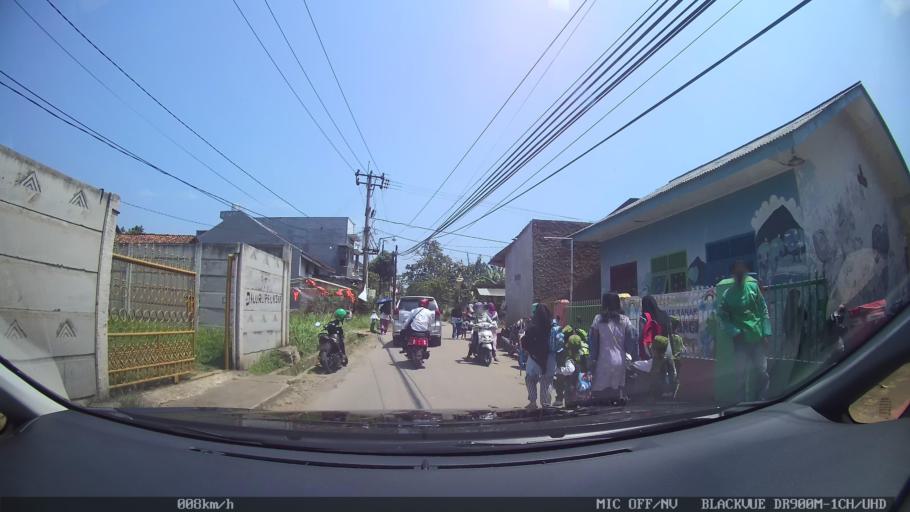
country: ID
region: Lampung
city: Kedaton
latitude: -5.3610
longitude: 105.2745
